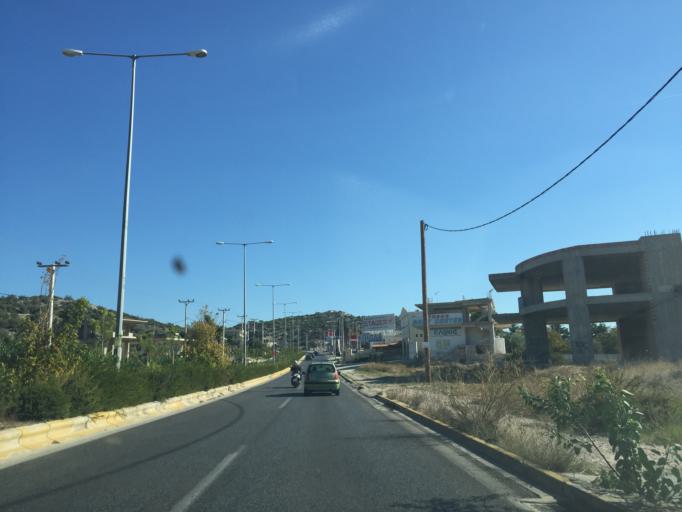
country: GR
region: Attica
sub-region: Nomarchia Anatolikis Attikis
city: Kitsi
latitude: 37.8576
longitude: 23.8372
